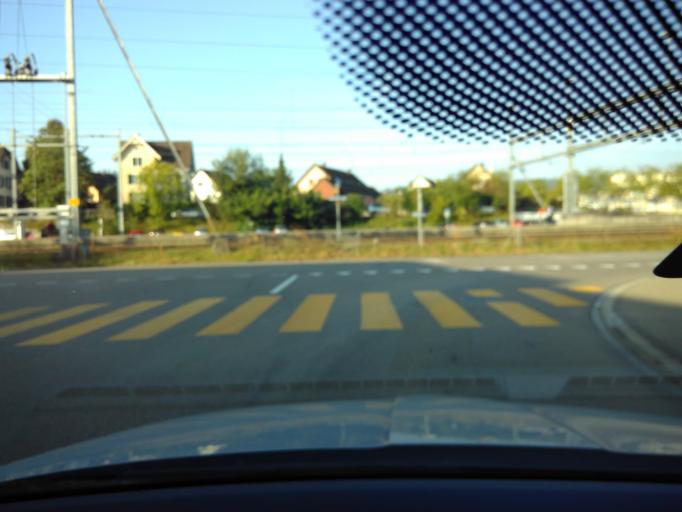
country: CH
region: Zurich
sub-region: Bezirk Dielsdorf
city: Regensdorf
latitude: 47.4377
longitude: 8.4713
